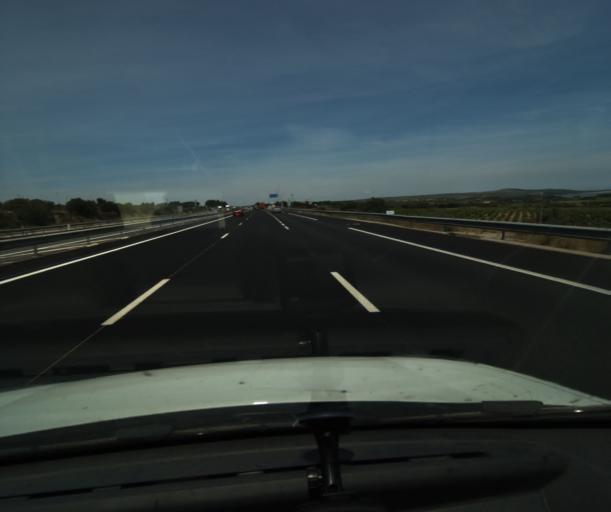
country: FR
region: Languedoc-Roussillon
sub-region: Departement de l'Aude
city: Leucate
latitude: 42.9455
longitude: 2.9708
